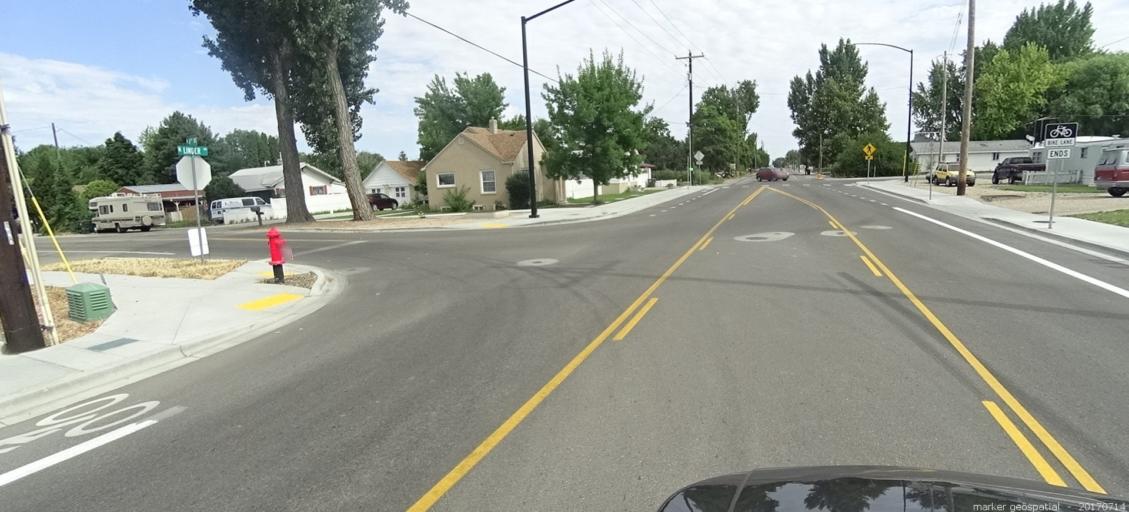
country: US
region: Idaho
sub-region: Ada County
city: Kuna
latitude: 43.4915
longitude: -116.4137
